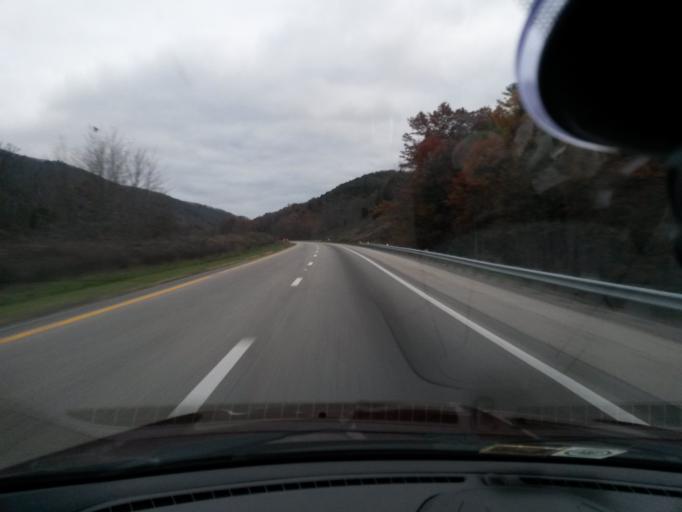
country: US
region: Virginia
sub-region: City of Lexington
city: Lexington
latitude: 37.8596
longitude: -79.6261
